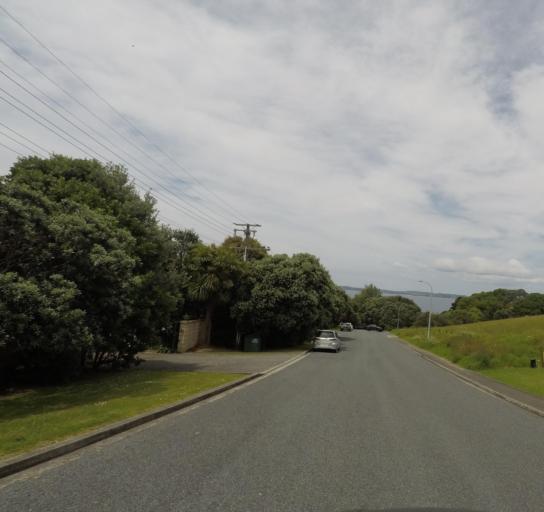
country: NZ
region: Auckland
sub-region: Auckland
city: Warkworth
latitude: -36.2956
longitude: 174.8023
